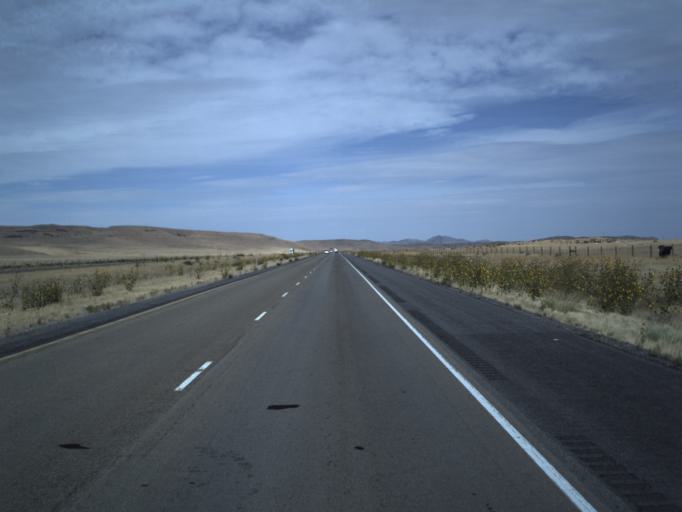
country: US
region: Utah
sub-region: Tooele County
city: Grantsville
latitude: 40.7908
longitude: -112.8322
